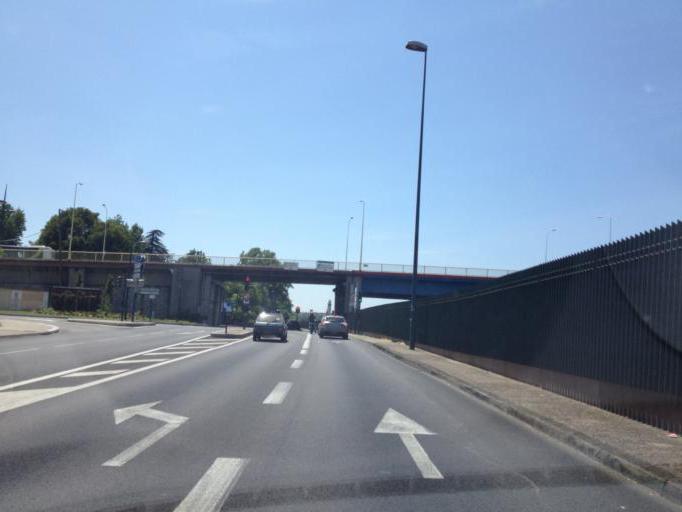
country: FR
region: Rhone-Alpes
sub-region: Departement de l'Ardeche
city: Guilherand-Granges
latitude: 44.9321
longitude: 4.8855
